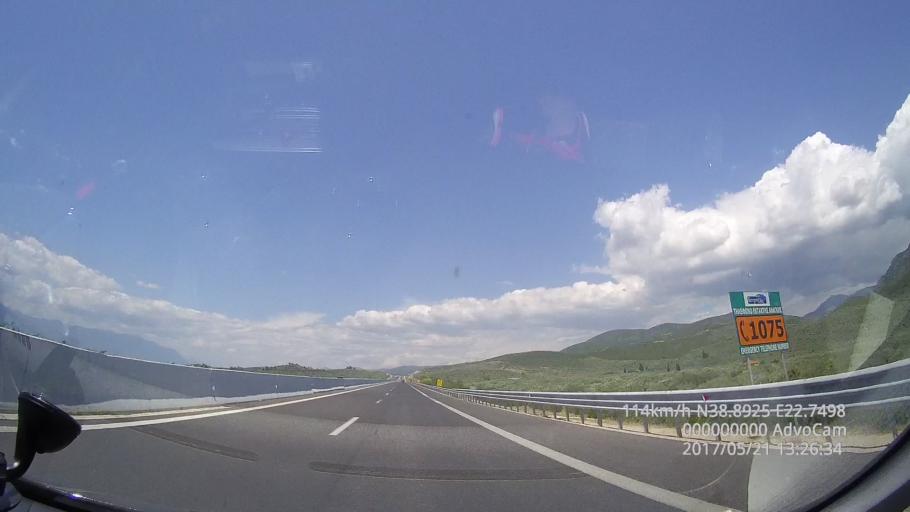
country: GR
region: Central Greece
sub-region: Nomos Fthiotidos
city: Kainouryion
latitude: 38.8927
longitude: 22.7492
